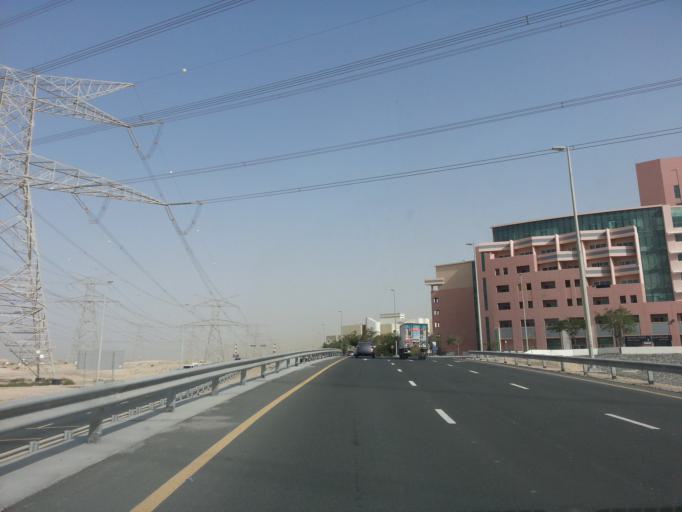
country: AE
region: Dubai
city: Dubai
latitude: 25.0516
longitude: 55.1332
